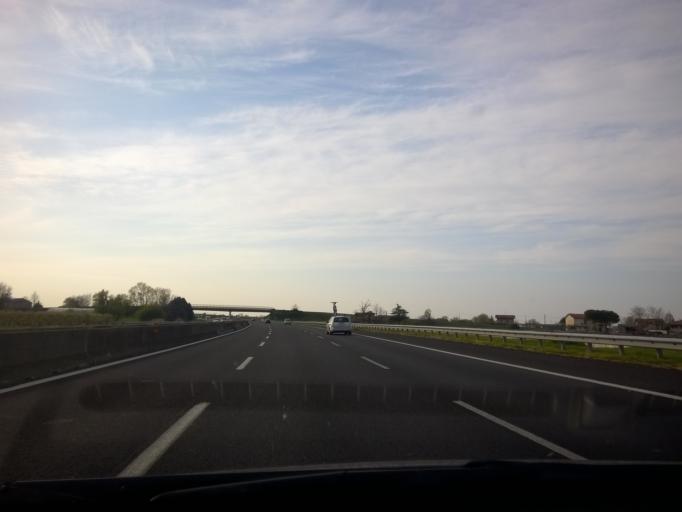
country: IT
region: Emilia-Romagna
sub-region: Forli-Cesena
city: Sala
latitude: 44.1324
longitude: 12.3718
